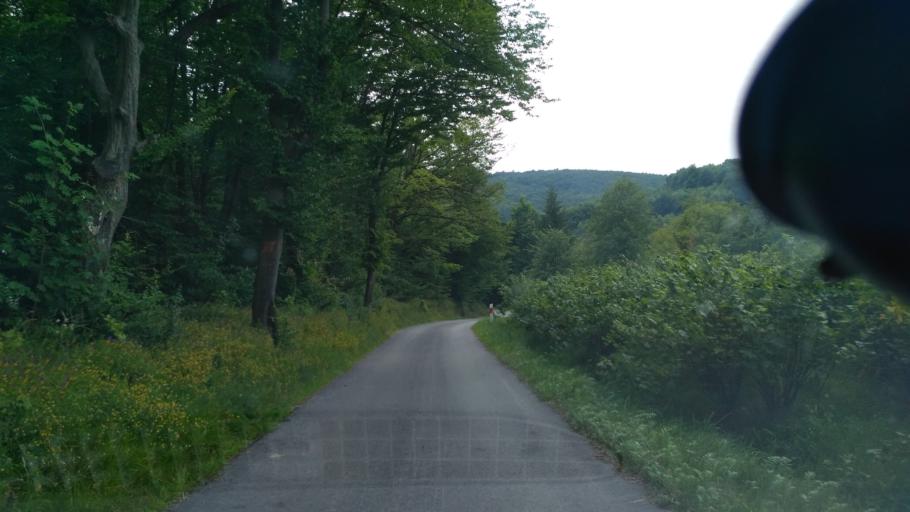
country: PL
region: Subcarpathian Voivodeship
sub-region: Powiat przeworski
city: Lopuszka Wielka
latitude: 49.9020
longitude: 22.4116
